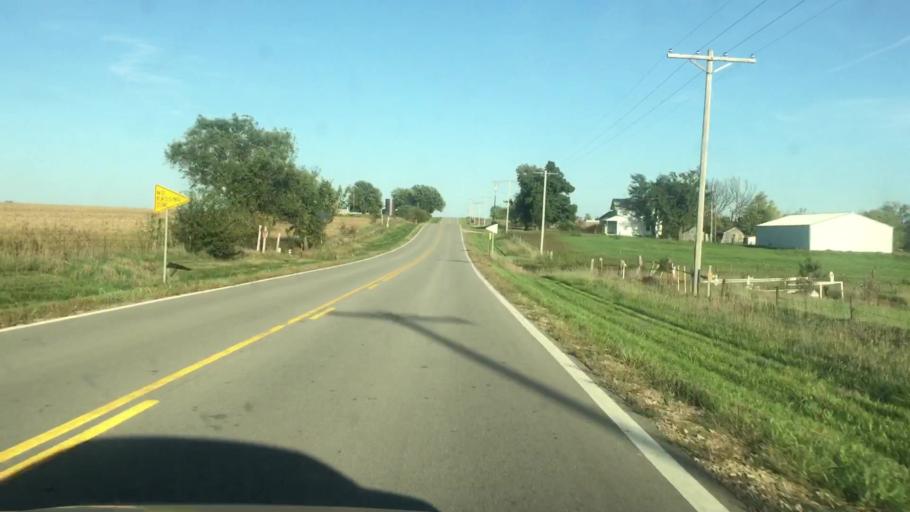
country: US
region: Kansas
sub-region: Brown County
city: Horton
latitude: 39.5876
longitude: -95.5905
